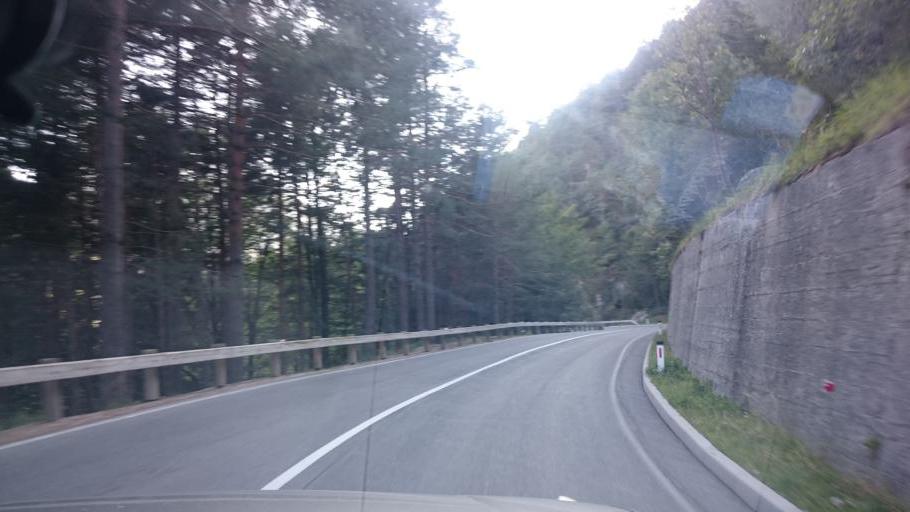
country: IT
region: Friuli Venezia Giulia
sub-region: Provincia di Udine
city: Tarvisio
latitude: 46.4229
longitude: 13.5936
